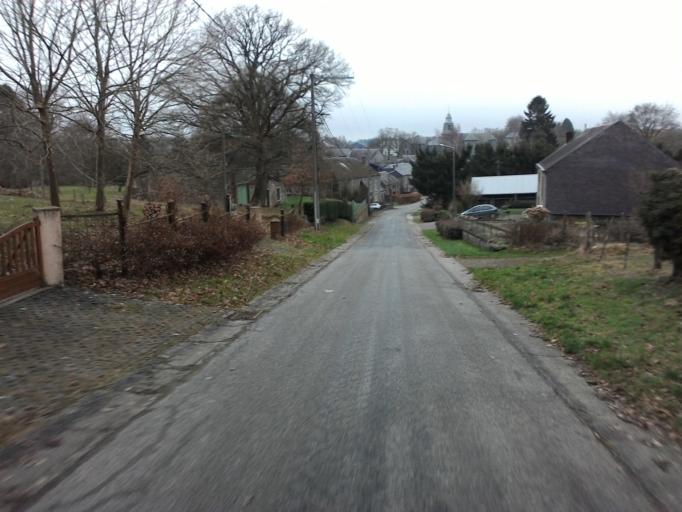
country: BE
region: Wallonia
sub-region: Province de Namur
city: Gedinne
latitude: 50.0200
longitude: 4.8686
